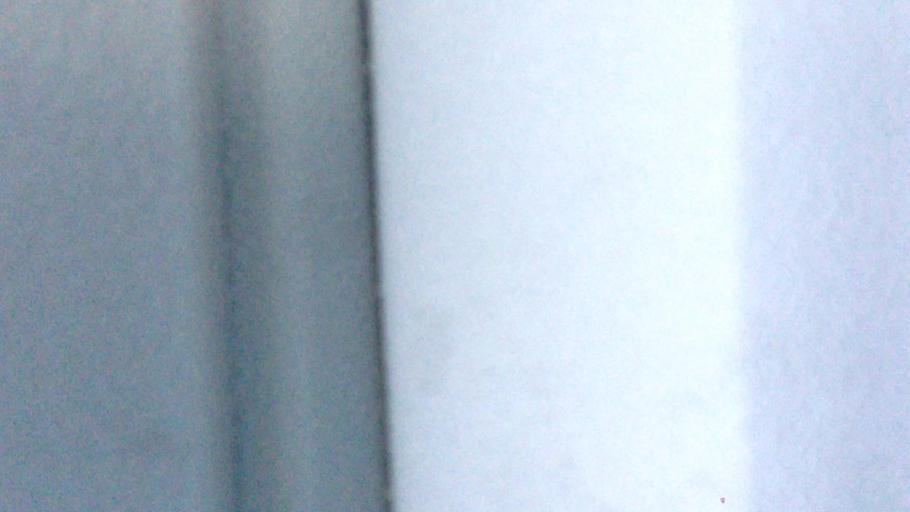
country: US
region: New York
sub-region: Dutchess County
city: Rhinebeck
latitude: 41.9696
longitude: -73.9211
